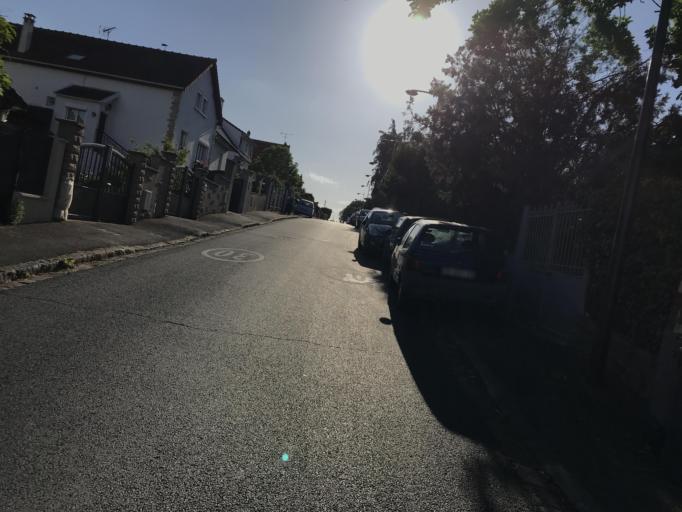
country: FR
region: Ile-de-France
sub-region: Departement de l'Essonne
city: Palaiseau
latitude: 48.7255
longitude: 2.2328
